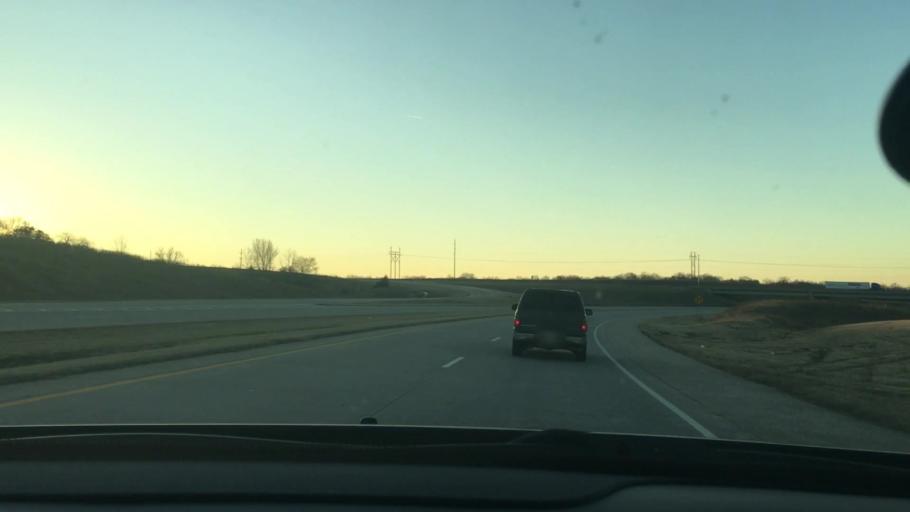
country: US
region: Oklahoma
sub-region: Pontotoc County
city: Ada
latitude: 34.7930
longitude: -96.6940
